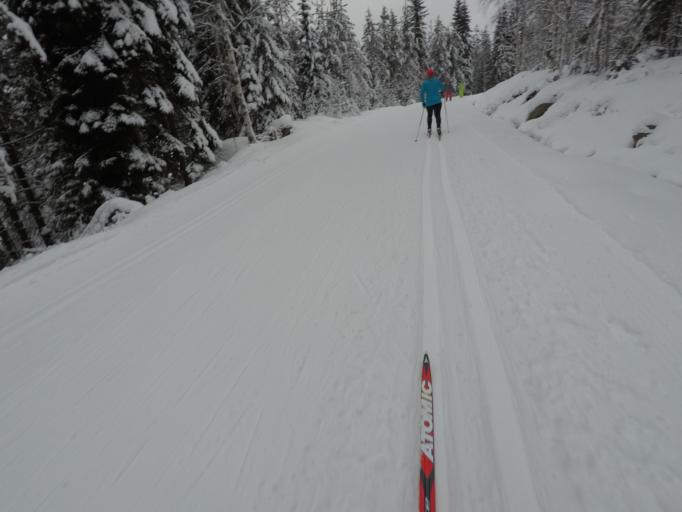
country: SE
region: Dalarna
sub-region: Ludvika Kommun
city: Abborrberget
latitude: 60.1372
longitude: 14.4839
